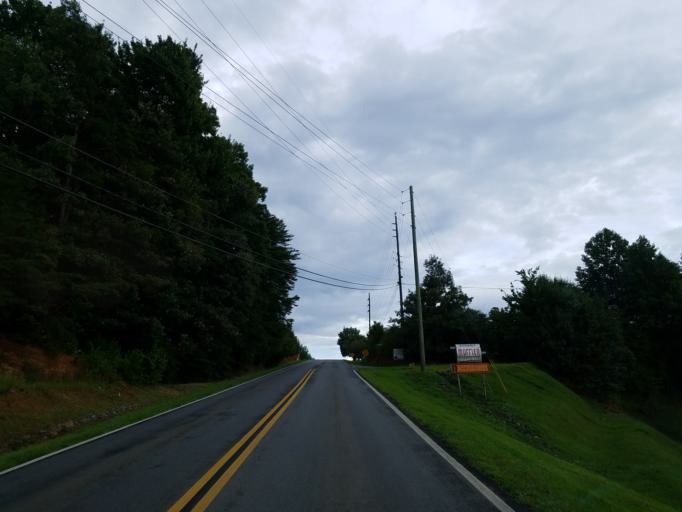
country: US
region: Georgia
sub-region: Gilmer County
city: Ellijay
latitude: 34.6795
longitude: -84.4834
